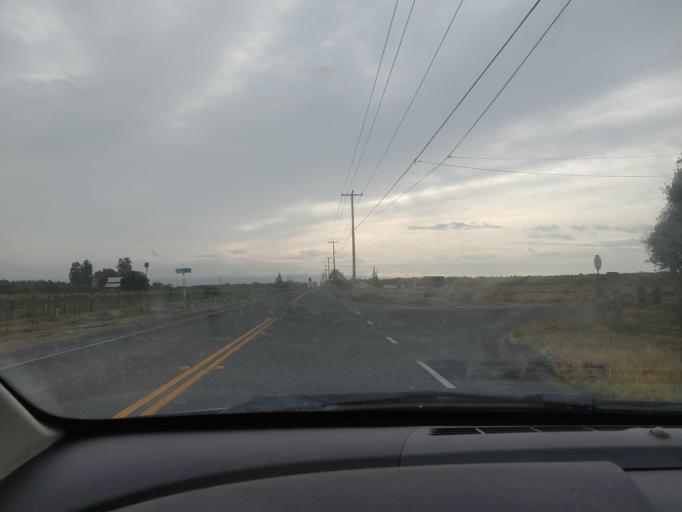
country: US
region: California
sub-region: Stanislaus County
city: Salida
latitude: 37.6818
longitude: -121.1004
